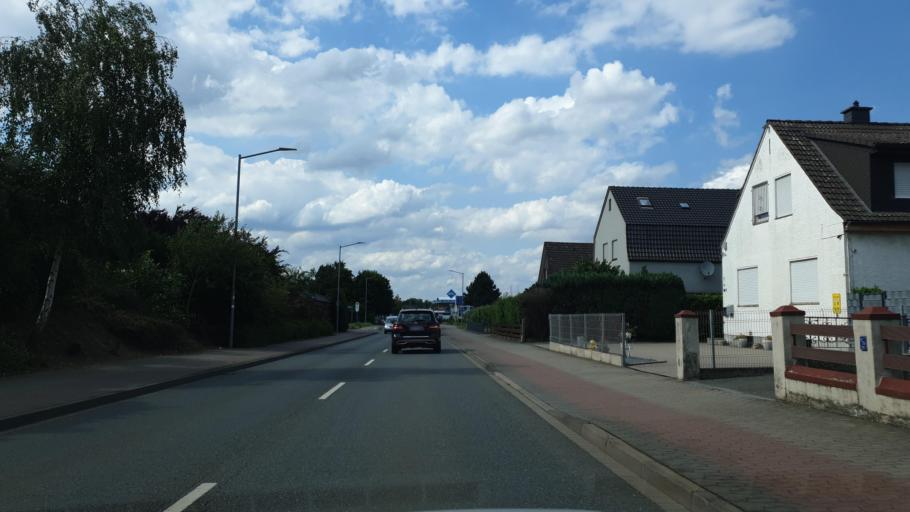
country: DE
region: North Rhine-Westphalia
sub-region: Regierungsbezirk Detmold
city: Hiddenhausen
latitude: 52.1836
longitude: 8.6050
